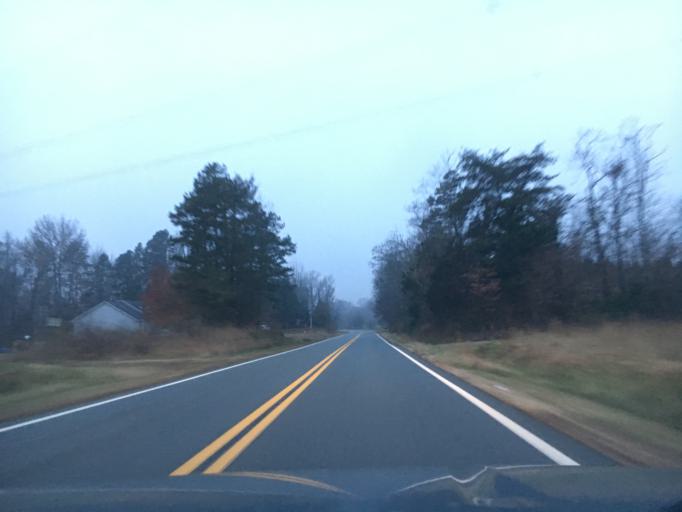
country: US
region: Virginia
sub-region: Halifax County
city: Mountain Road
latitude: 36.6884
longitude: -78.9837
